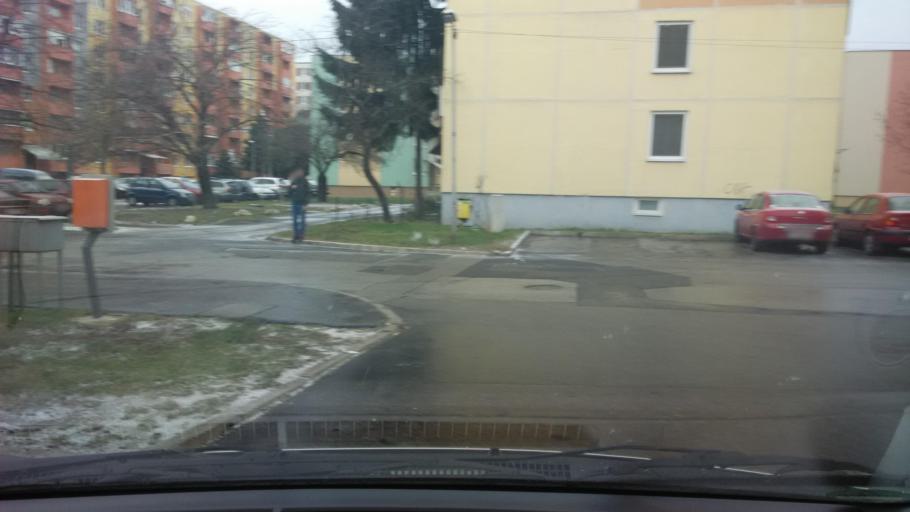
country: SK
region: Nitriansky
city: Levice
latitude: 48.2093
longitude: 18.6045
